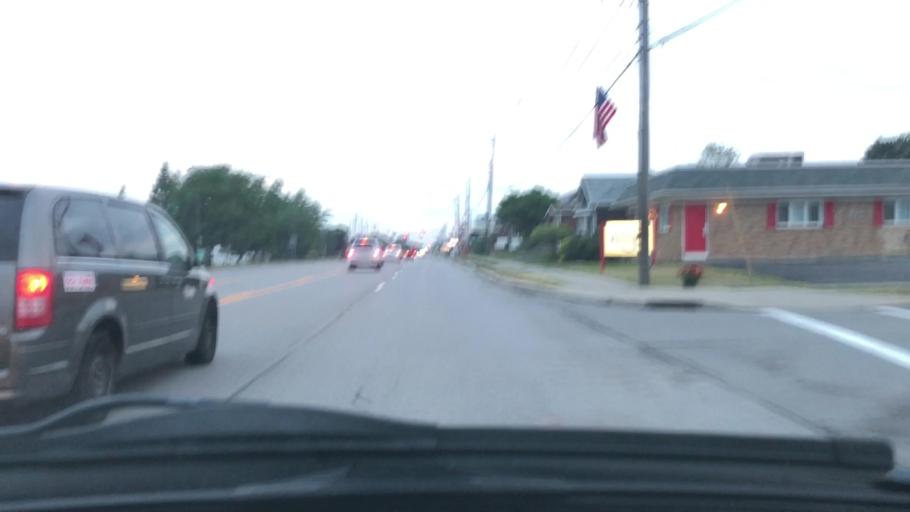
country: US
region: New York
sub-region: Erie County
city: Sloan
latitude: 42.9155
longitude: -78.7842
